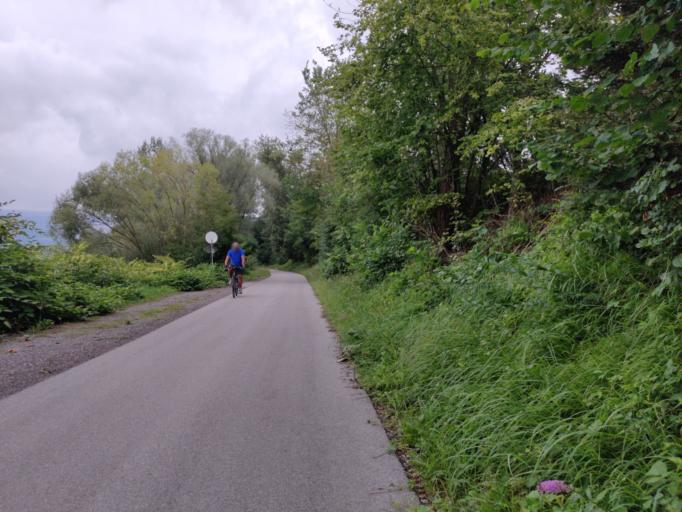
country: AT
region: Lower Austria
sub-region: Politischer Bezirk Melk
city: Ybbs an der Donau
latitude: 48.1789
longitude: 15.1210
